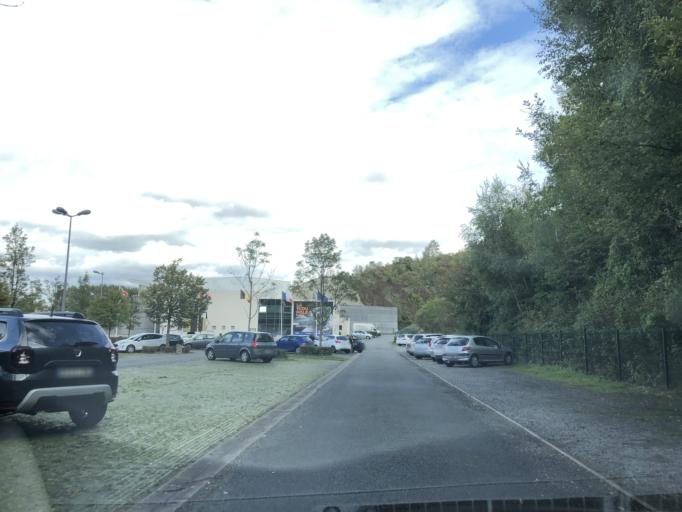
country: FR
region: Nord-Pas-de-Calais
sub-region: Departement du Pas-de-Calais
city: Wizernes
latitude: 50.7051
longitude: 2.2404
